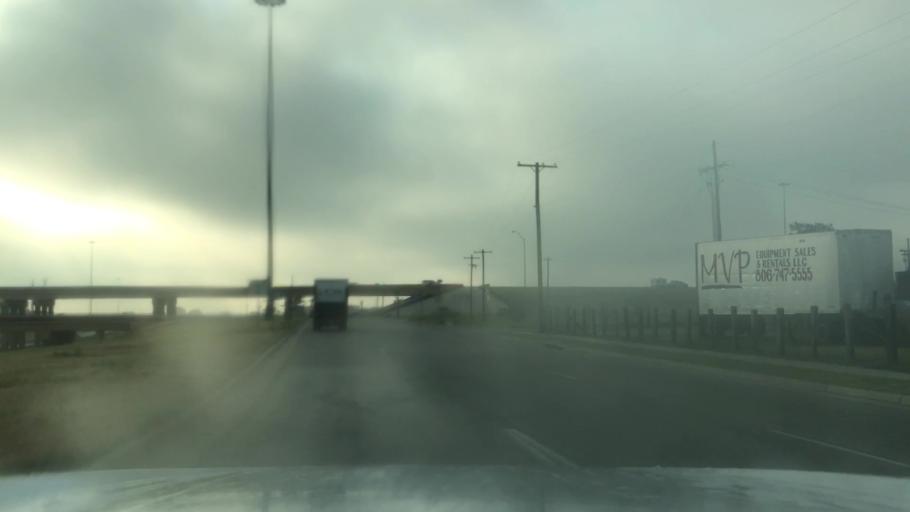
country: US
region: Texas
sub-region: Lubbock County
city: Lubbock
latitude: 33.5911
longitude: -101.8414
